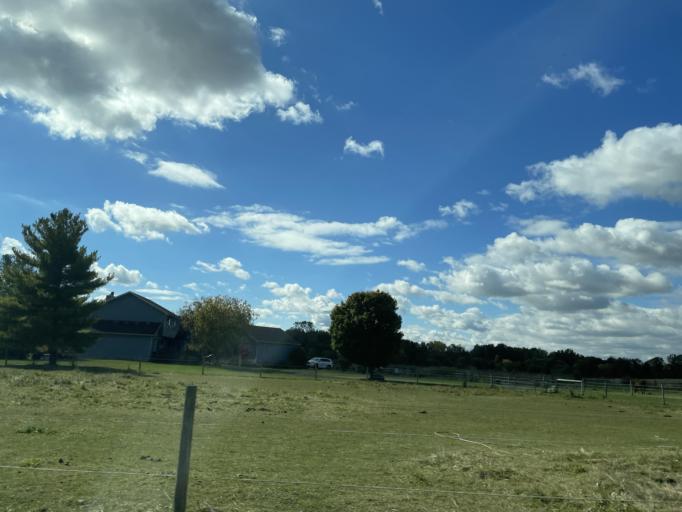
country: US
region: Indiana
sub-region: Whitley County
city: Churubusco
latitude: 41.1193
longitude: -85.2649
